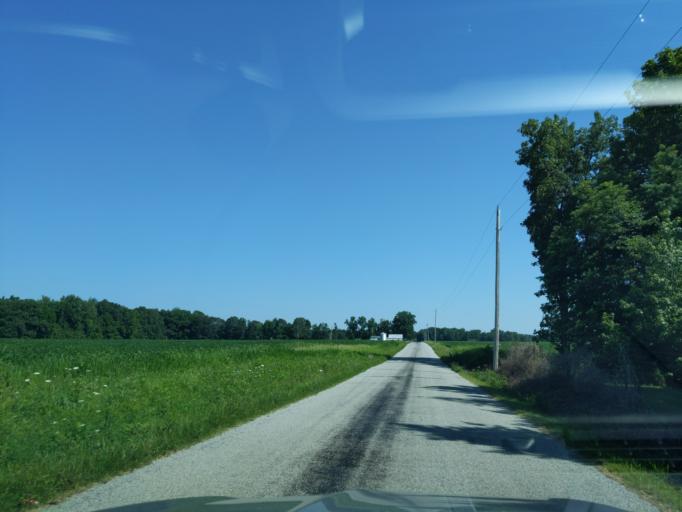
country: US
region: Indiana
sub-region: Ripley County
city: Osgood
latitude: 39.1063
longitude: -85.4322
